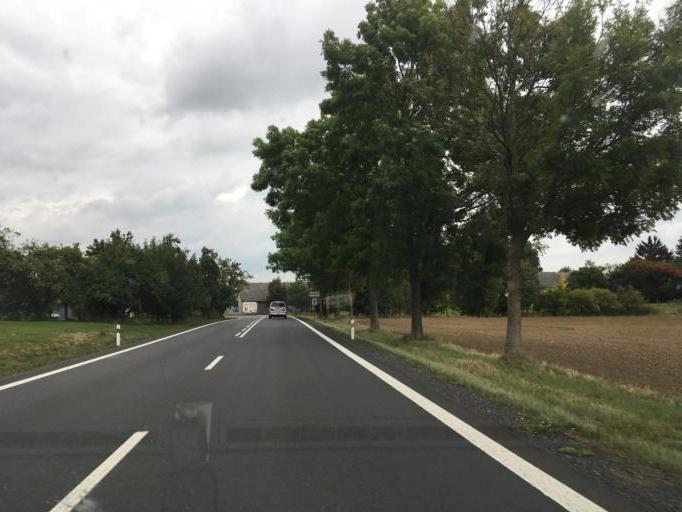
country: CZ
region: Vysocina
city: Horni Cerekev
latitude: 49.3462
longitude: 15.2930
